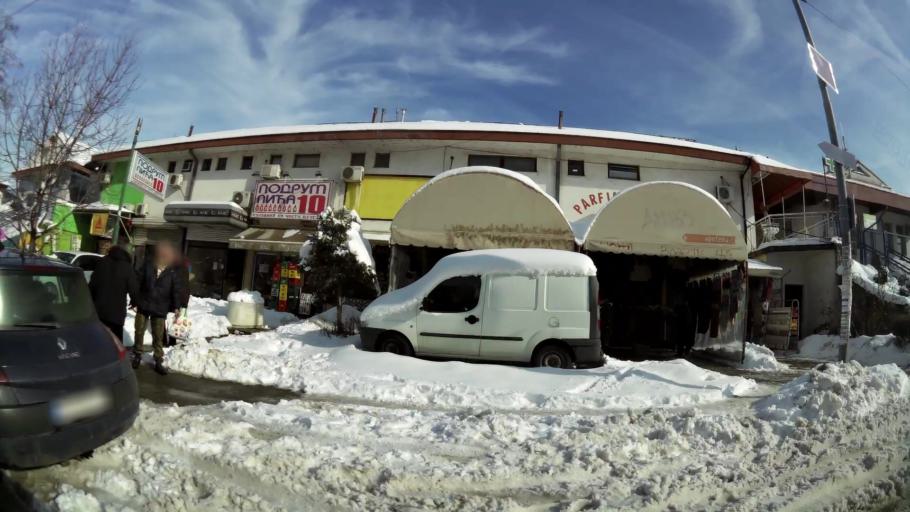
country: RS
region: Central Serbia
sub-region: Belgrade
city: Zvezdara
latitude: 44.7901
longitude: 20.5377
